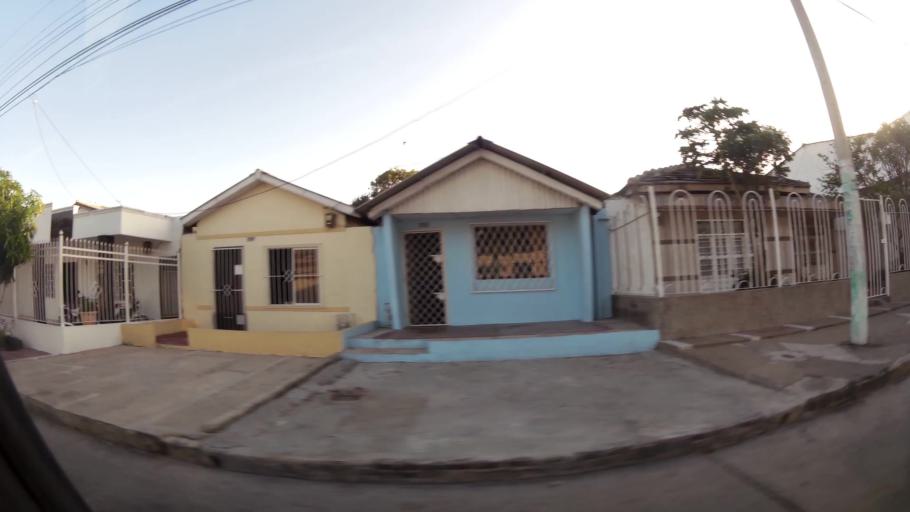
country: CO
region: Atlantico
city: Barranquilla
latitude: 10.9728
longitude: -74.8111
